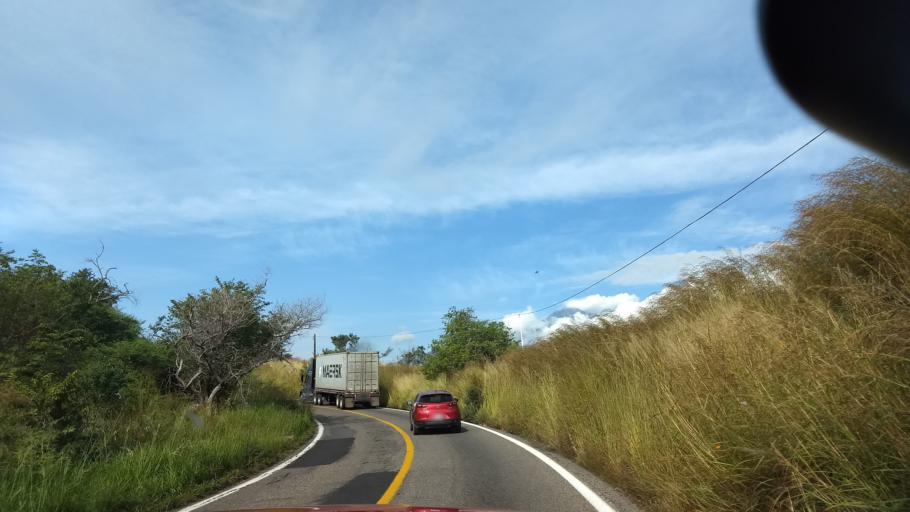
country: MX
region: Jalisco
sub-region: Tonila
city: San Marcos
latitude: 19.4449
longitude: -103.4832
